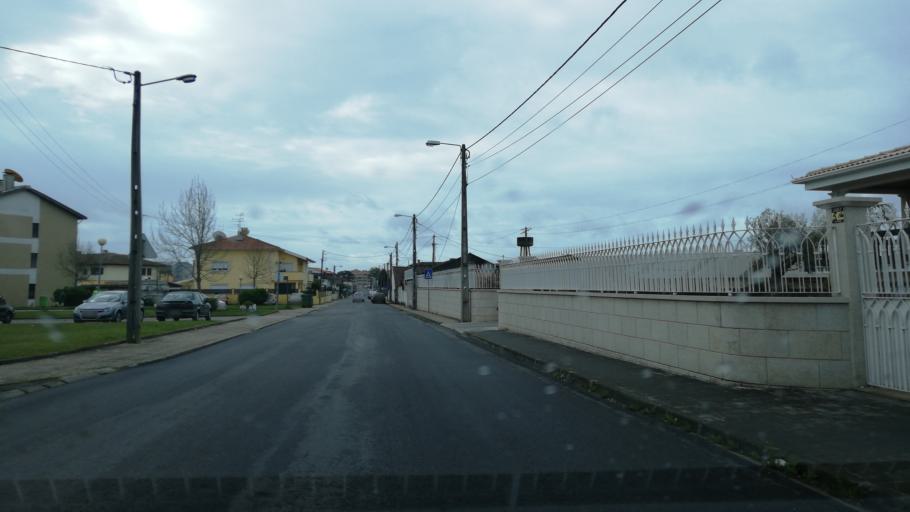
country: PT
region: Aveiro
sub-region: Agueda
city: Agueda
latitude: 40.5953
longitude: -8.4507
